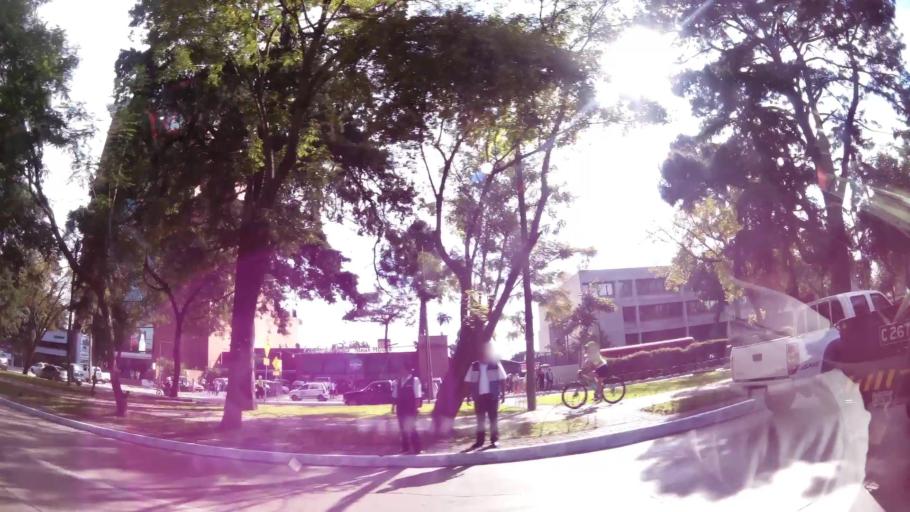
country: GT
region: Guatemala
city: Guatemala City
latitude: 14.6074
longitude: -90.5154
